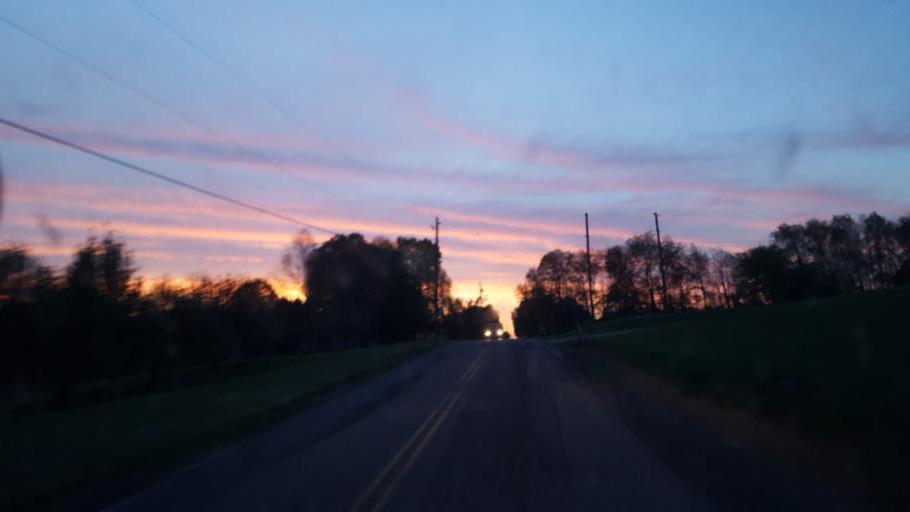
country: US
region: Ohio
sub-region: Knox County
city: Fredericktown
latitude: 40.4787
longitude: -82.5267
